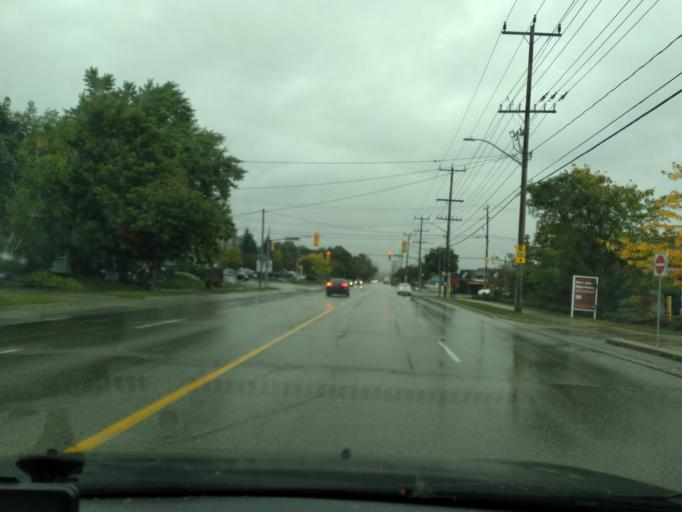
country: CA
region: Ontario
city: Barrie
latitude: 44.4111
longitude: -79.6899
